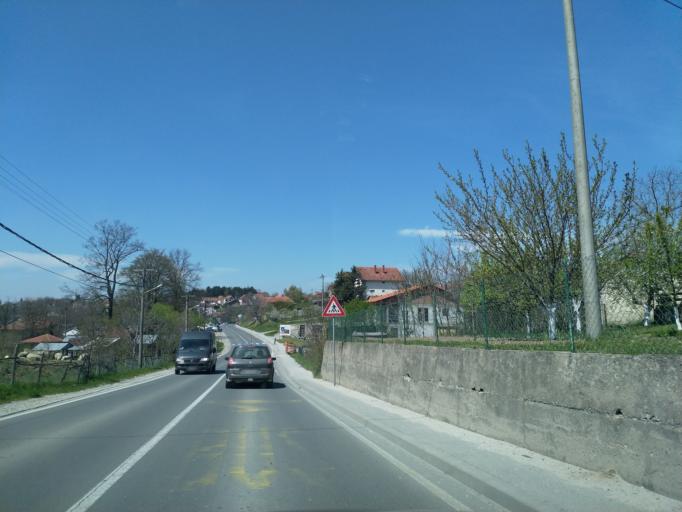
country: RS
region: Central Serbia
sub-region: Sumadijski Okrug
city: Arangelovac
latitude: 44.3269
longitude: 20.5236
